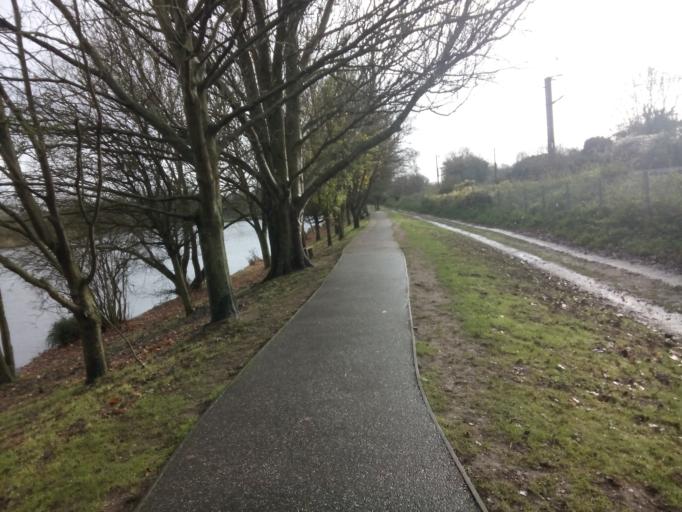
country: GB
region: England
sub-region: Suffolk
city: Needham Market
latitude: 52.1518
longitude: 1.0570
